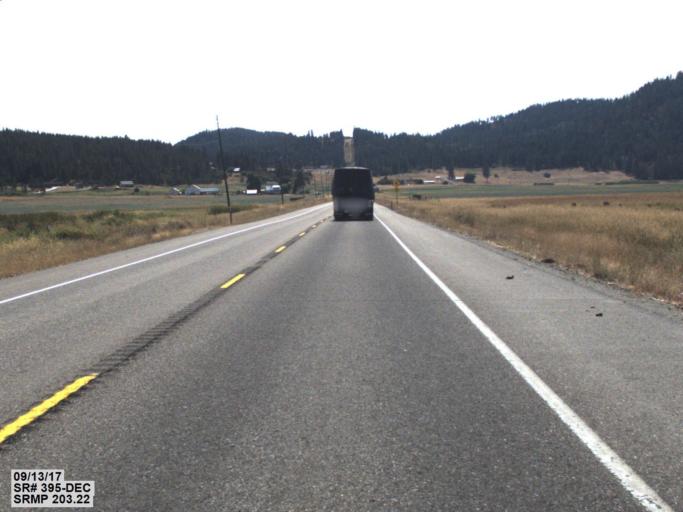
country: US
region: Washington
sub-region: Stevens County
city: Chewelah
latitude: 48.2197
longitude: -117.7154
